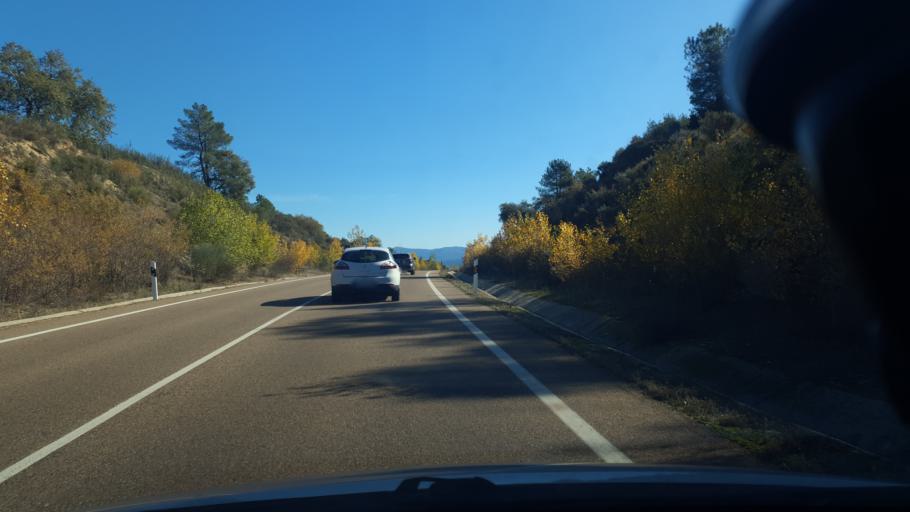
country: ES
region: Castille and Leon
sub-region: Provincia de Avila
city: Arenas de San Pedro
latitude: 40.1898
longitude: -5.0708
